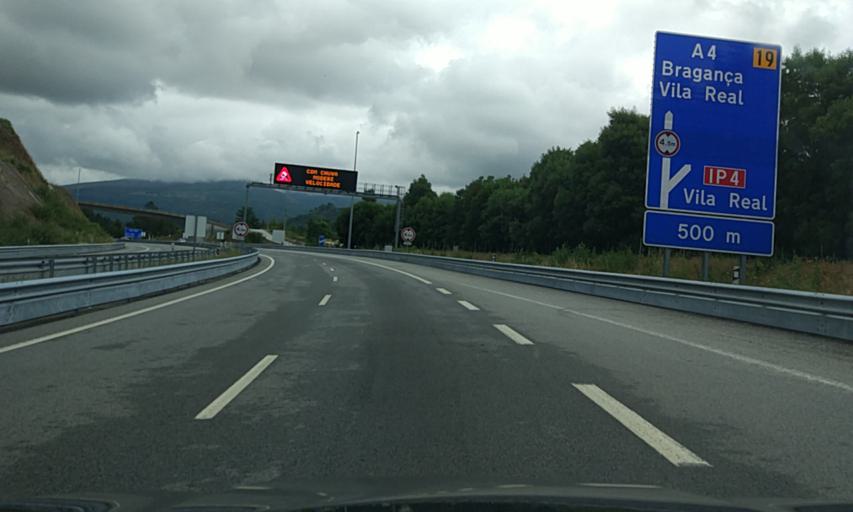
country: PT
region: Porto
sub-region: Amarante
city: Amarante
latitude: 41.2578
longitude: -8.0391
